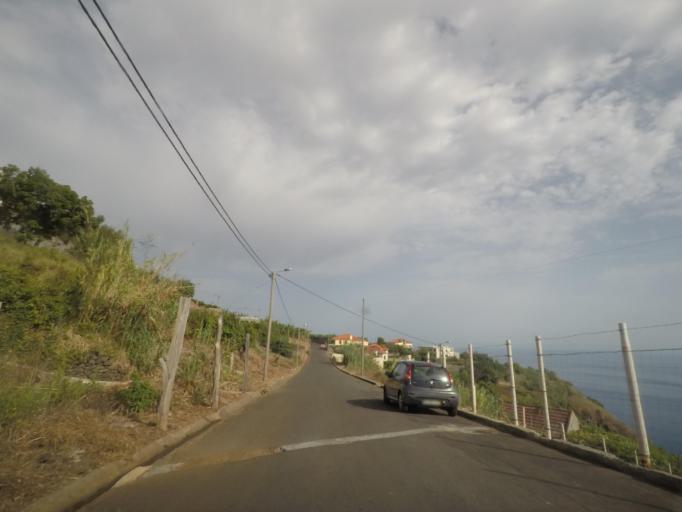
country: PT
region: Madeira
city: Ponta do Sol
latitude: 32.6946
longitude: -17.1188
